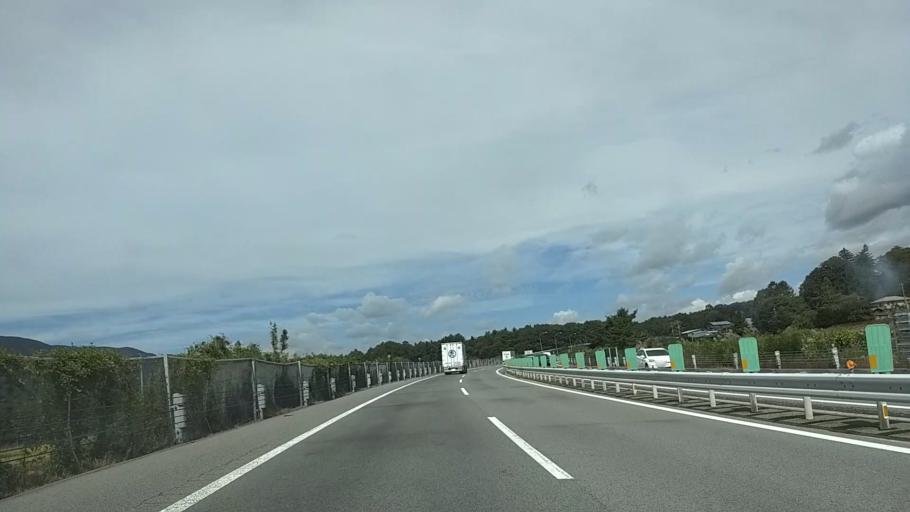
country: JP
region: Nagano
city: Chino
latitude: 35.9055
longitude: 138.2597
